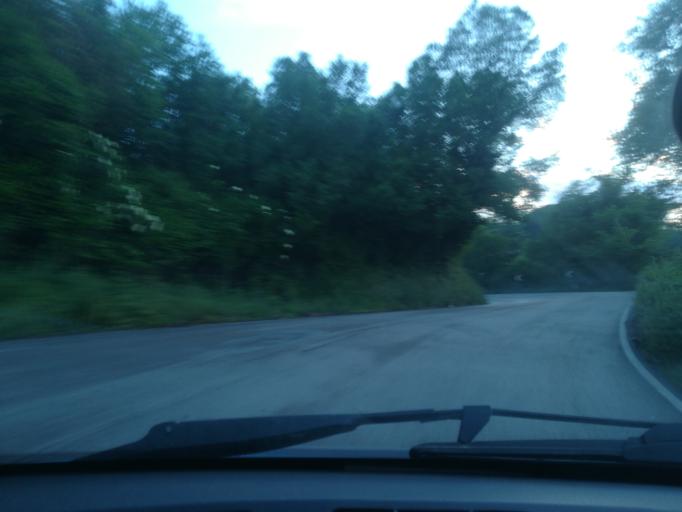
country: IT
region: The Marches
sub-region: Provincia di Macerata
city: Treia
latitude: 43.3147
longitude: 13.3084
